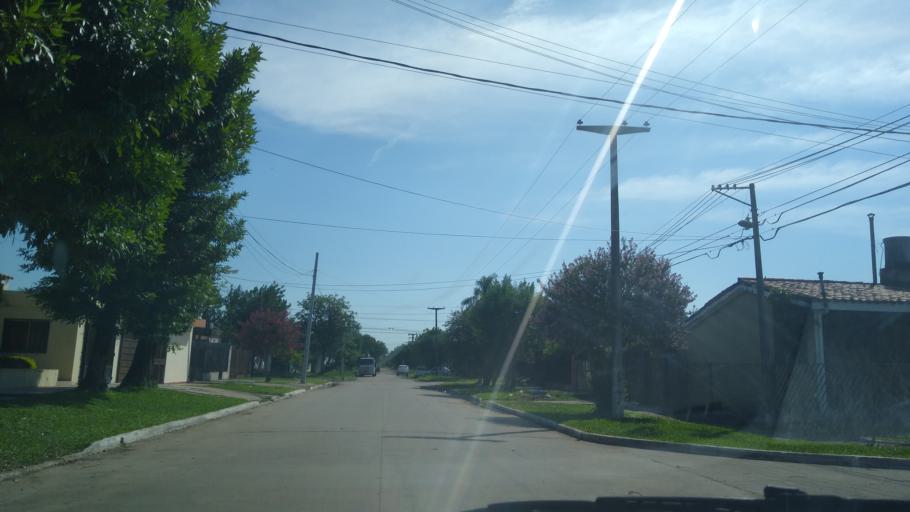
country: AR
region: Chaco
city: Barranqueras
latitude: -27.4851
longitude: -58.9508
